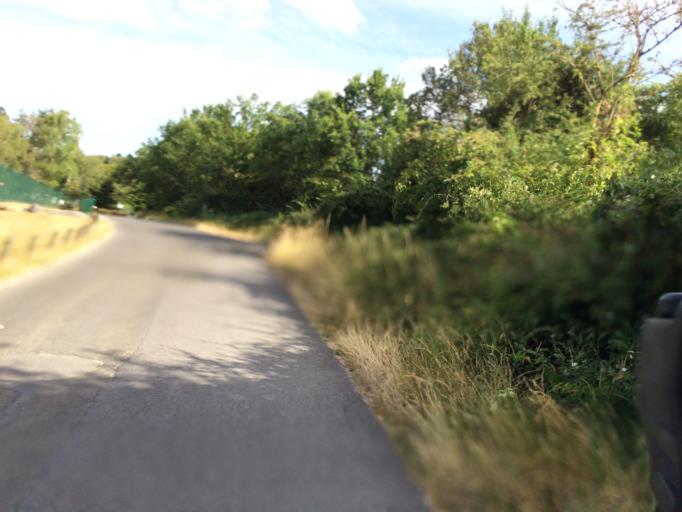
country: FR
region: Ile-de-France
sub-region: Departement de l'Essonne
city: Tigery
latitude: 48.6455
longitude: 2.4977
